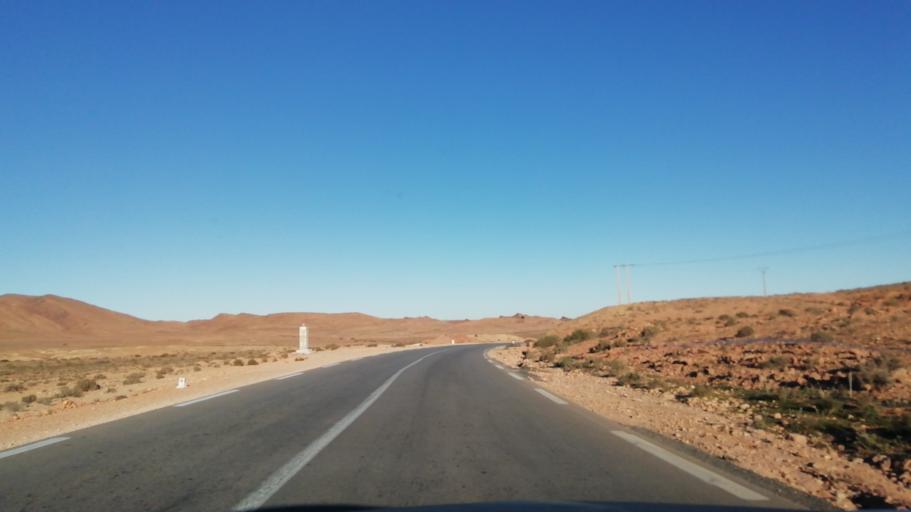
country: DZ
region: El Bayadh
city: El Abiodh Sidi Cheikh
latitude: 33.1743
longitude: 0.4464
